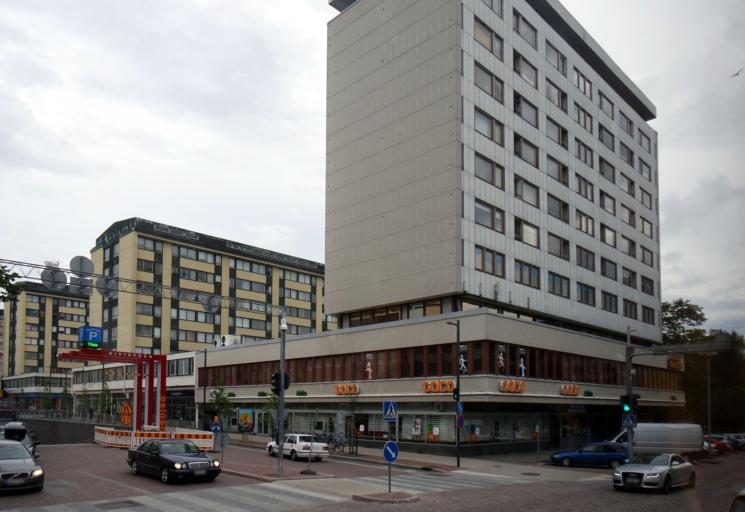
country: FI
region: Northern Ostrobothnia
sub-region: Oulu
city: Oulu
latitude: 65.0130
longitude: 25.4771
